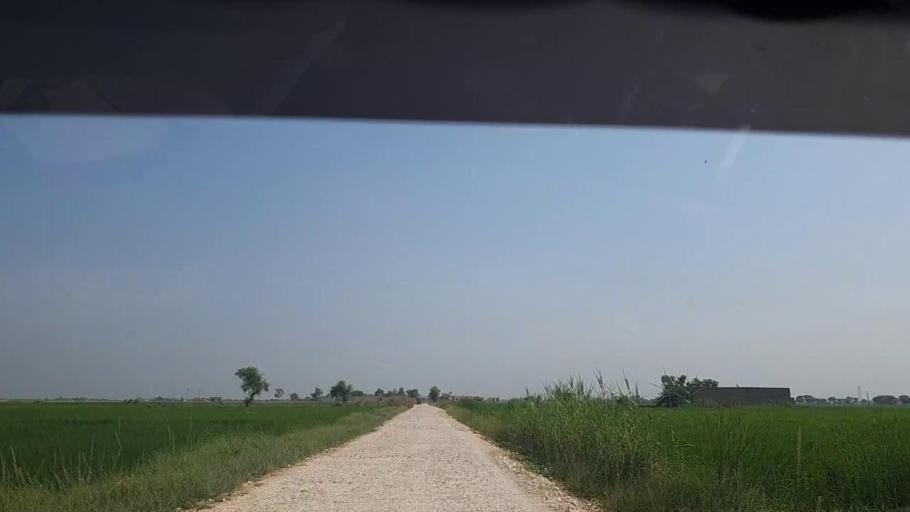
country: PK
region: Sindh
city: Thul
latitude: 28.1977
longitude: 68.7317
